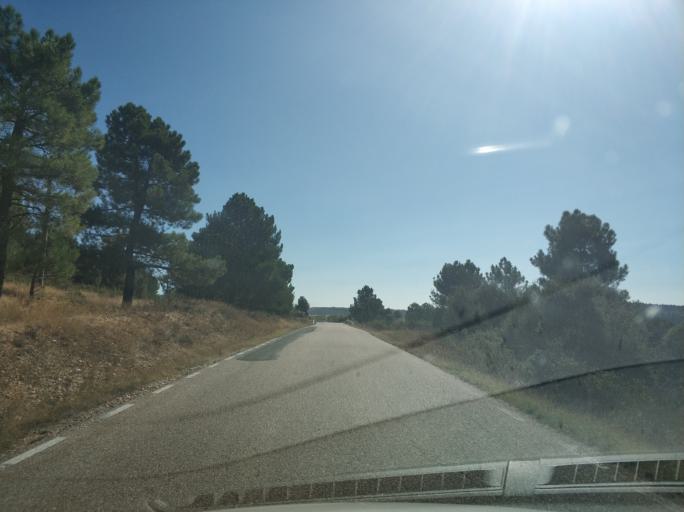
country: ES
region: Castille and Leon
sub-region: Provincia de Soria
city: Santa Maria de las Hoyas
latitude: 41.7755
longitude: -3.1788
